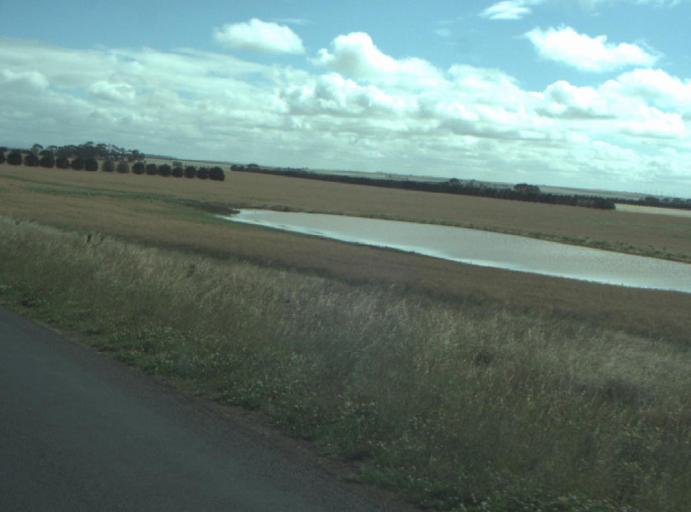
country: AU
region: Victoria
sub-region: Greater Geelong
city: Lara
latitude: -37.9348
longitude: 144.3109
